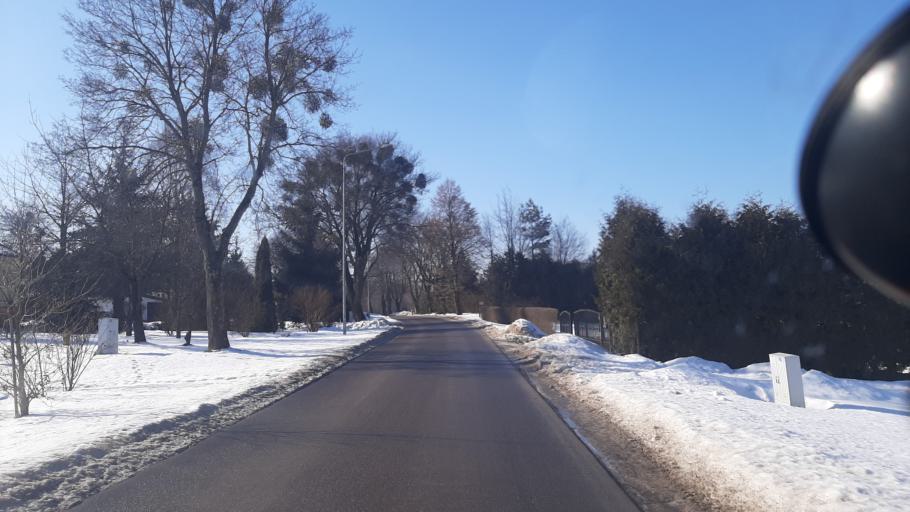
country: PL
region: Lublin Voivodeship
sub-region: Powiat pulawski
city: Naleczow
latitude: 51.2957
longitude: 22.2322
